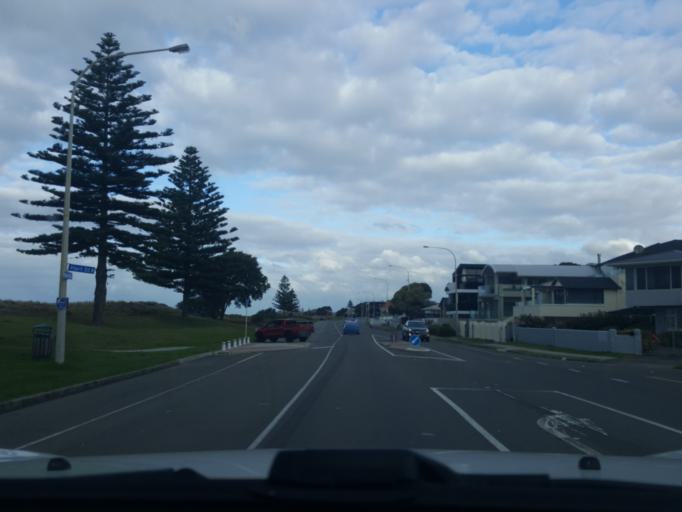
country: NZ
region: Bay of Plenty
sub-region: Tauranga City
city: Tauranga
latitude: -37.6518
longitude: 176.2046
